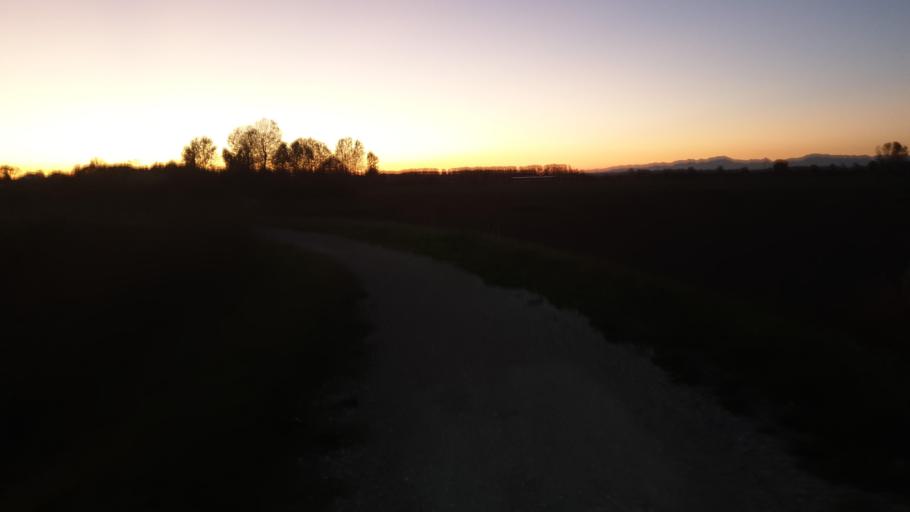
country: IT
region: Veneto
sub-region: Provincia di Venezia
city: Fiesso d'Artico
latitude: 45.4275
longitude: 12.0261
